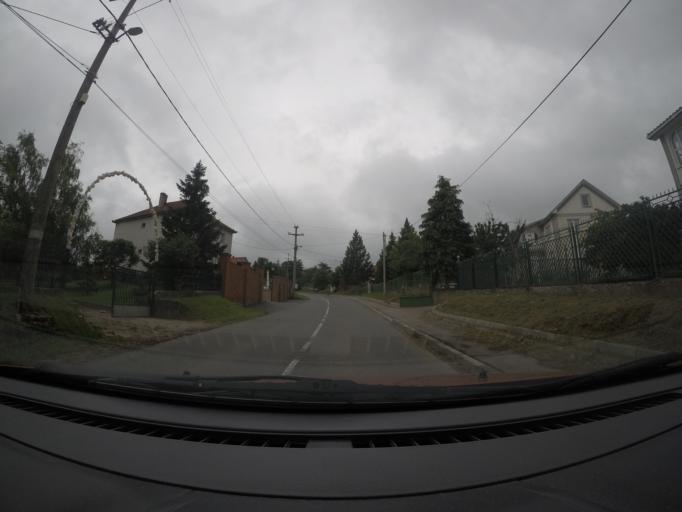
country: RS
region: Central Serbia
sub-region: Belgrade
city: Zvezdara
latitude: 44.6975
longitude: 20.5556
